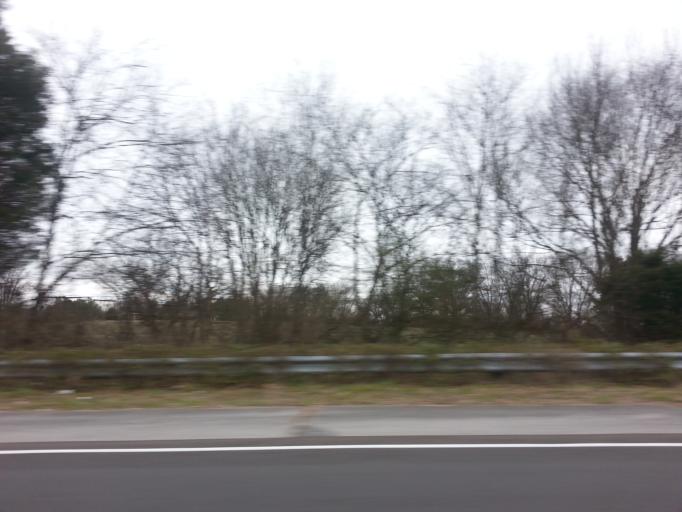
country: US
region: Tennessee
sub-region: Jefferson County
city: Jefferson City
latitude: 36.1369
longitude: -83.4705
